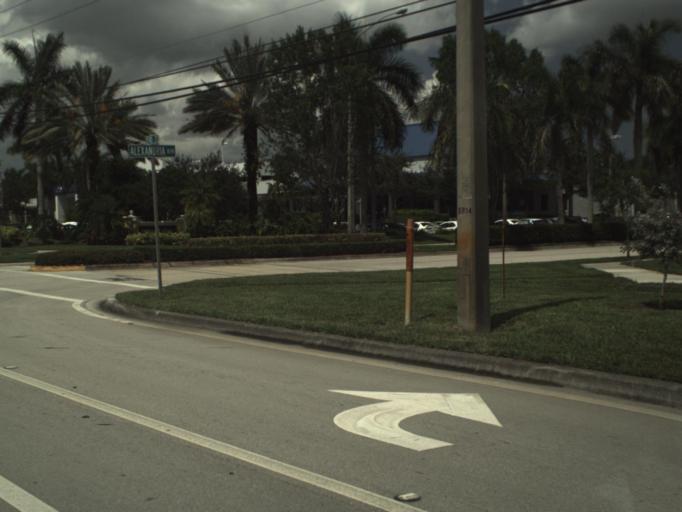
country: US
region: Florida
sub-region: Broward County
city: Parkland
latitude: 26.2905
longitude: -80.2019
